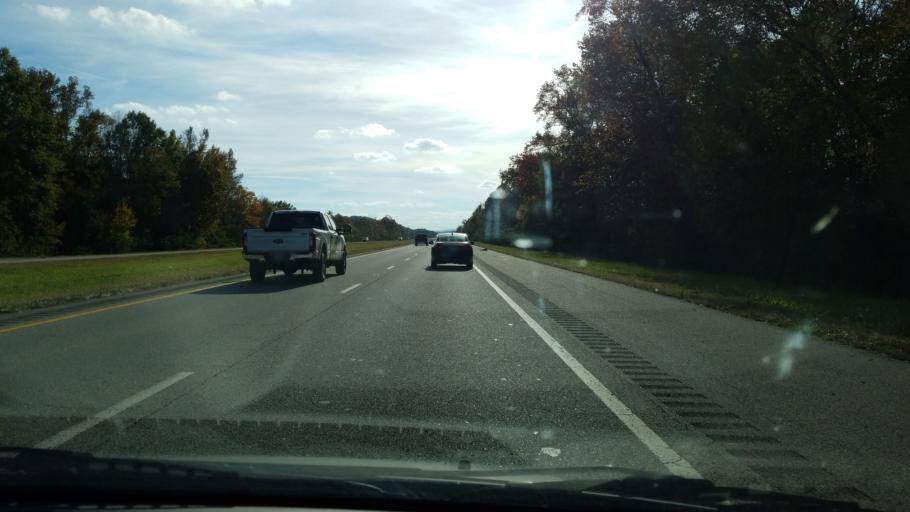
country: US
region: Tennessee
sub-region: Hamilton County
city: Soddy-Daisy
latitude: 35.2286
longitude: -85.2026
